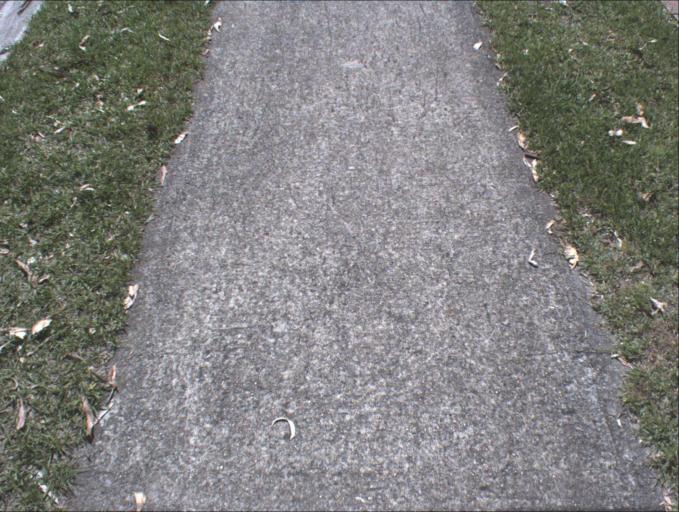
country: AU
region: Queensland
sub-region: Logan
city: Waterford West
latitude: -27.7056
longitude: 153.1637
